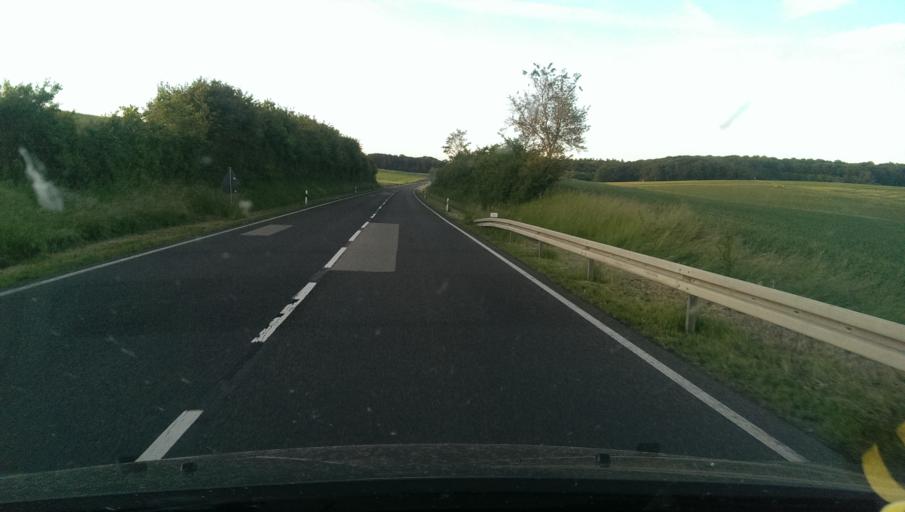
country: DE
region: Bavaria
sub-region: Regierungsbezirk Unterfranken
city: Waldbrunn
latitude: 49.7111
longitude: 9.7908
